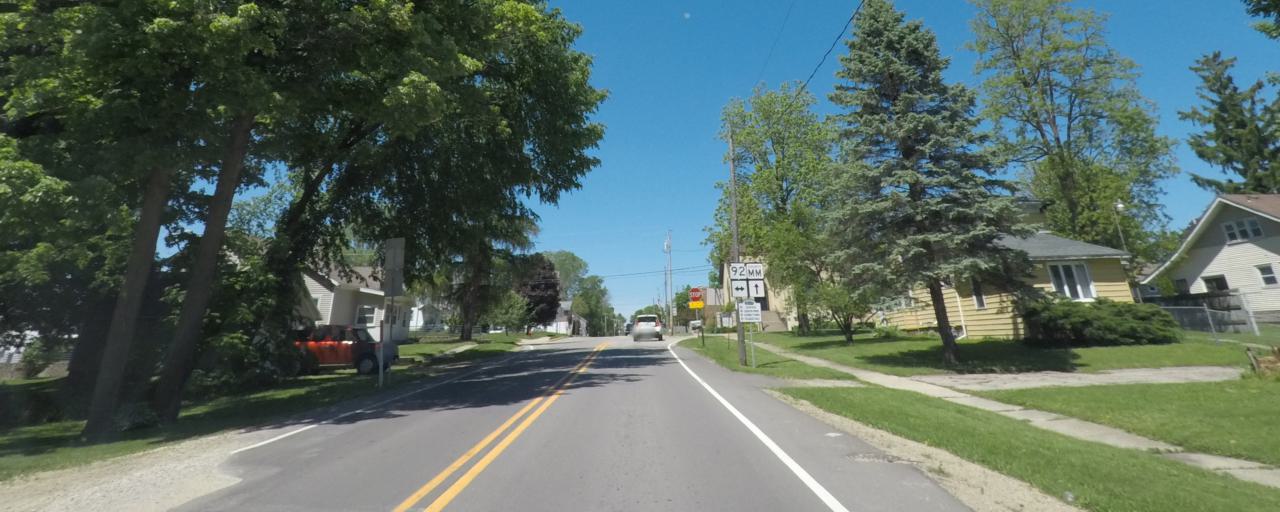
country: US
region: Wisconsin
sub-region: Green County
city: Brooklyn
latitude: 42.8517
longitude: -89.3691
